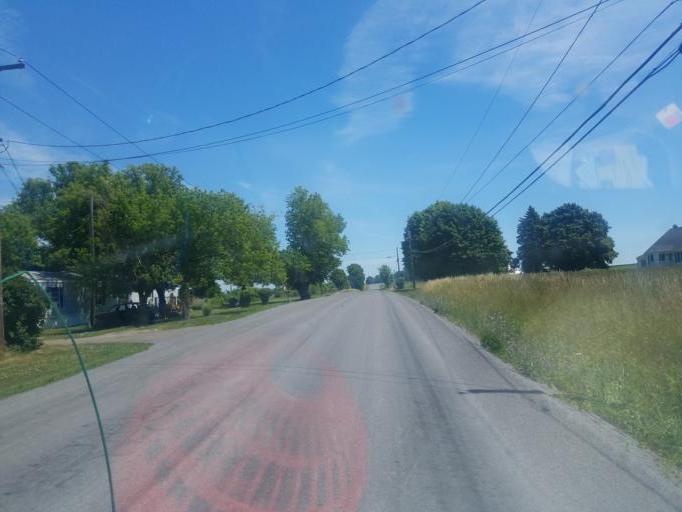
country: US
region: New York
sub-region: Yates County
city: Penn Yan
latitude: 42.6523
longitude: -77.0283
